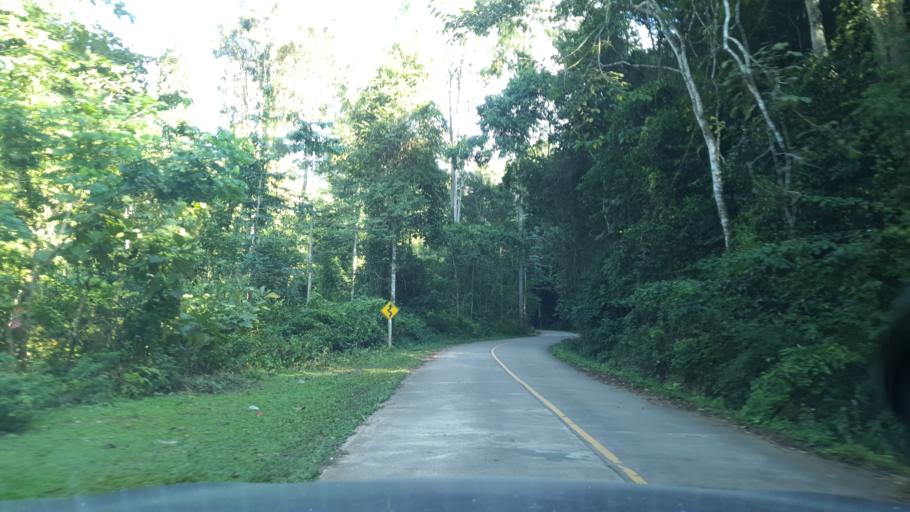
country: TH
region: Chiang Mai
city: Wiang Haeng
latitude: 19.3788
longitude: 98.7464
